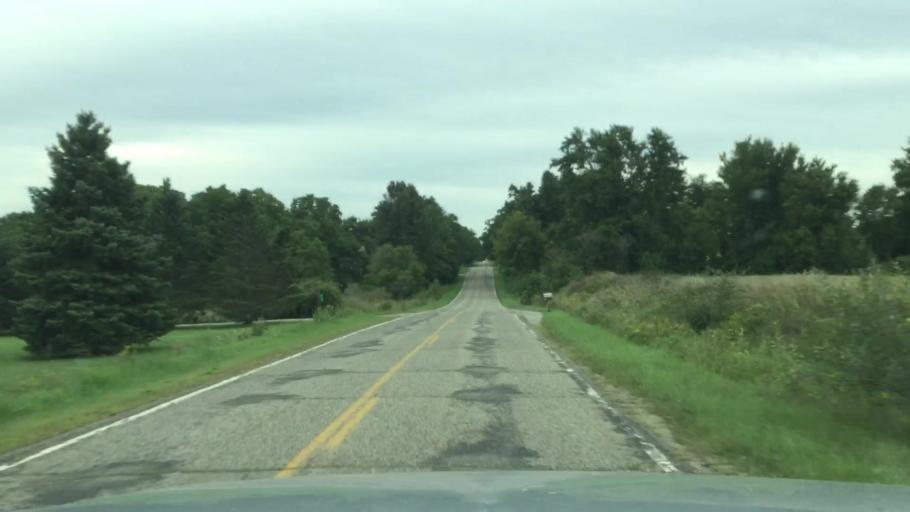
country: US
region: Michigan
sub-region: Shiawassee County
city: Durand
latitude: 42.8991
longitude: -84.0692
